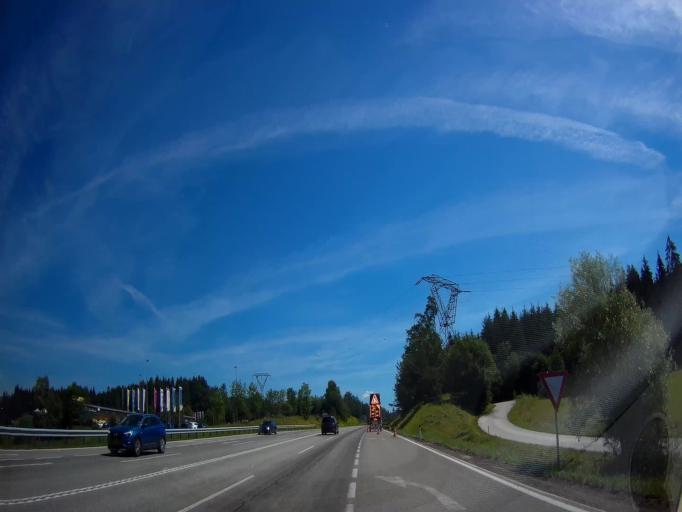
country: AT
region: Carinthia
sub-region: Politischer Bezirk Sankt Veit an der Glan
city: St. Georgen am Laengsee
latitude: 46.8059
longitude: 14.4127
